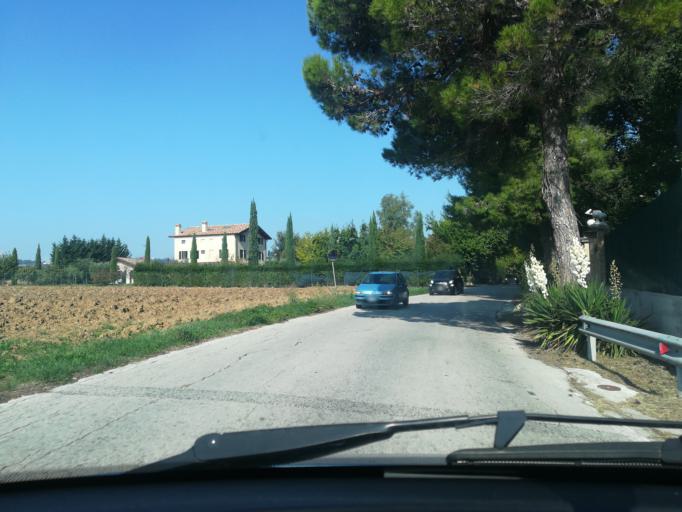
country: IT
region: The Marches
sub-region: Provincia di Macerata
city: Macerata
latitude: 43.2686
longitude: 13.4514
